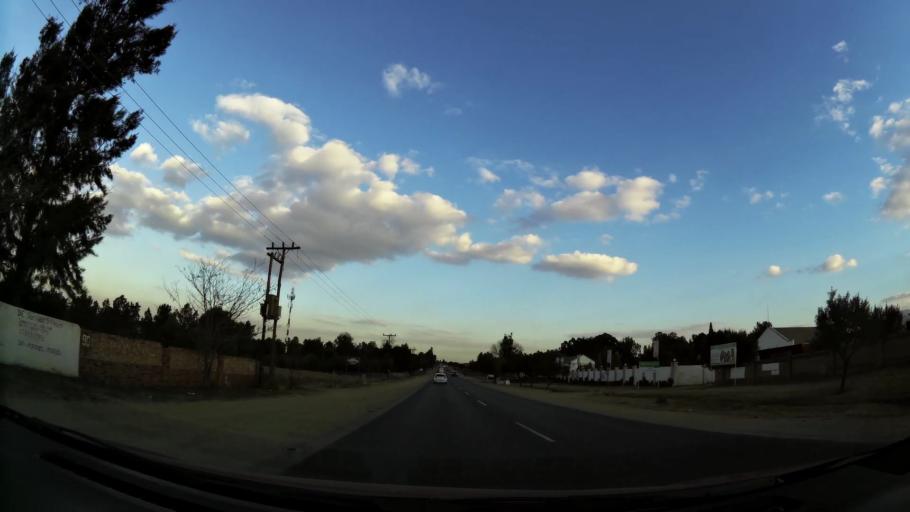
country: ZA
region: Gauteng
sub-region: City of Johannesburg Metropolitan Municipality
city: Midrand
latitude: -25.9975
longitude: 28.1556
